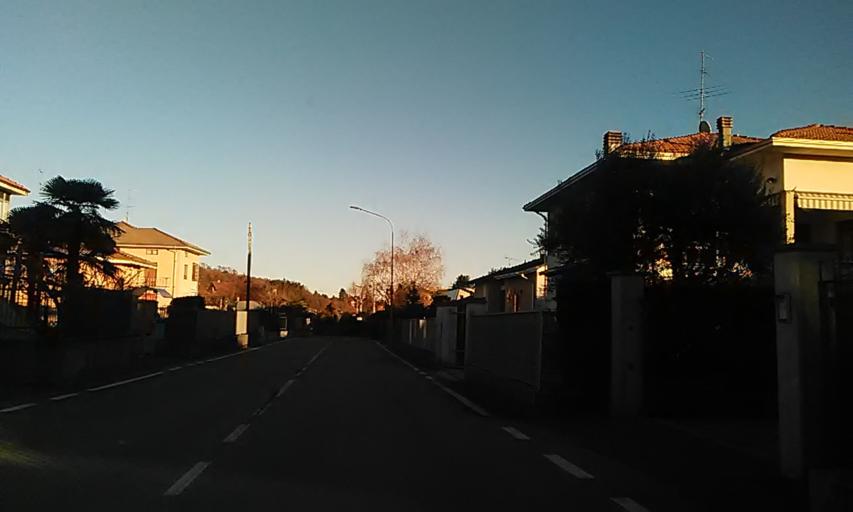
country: IT
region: Piedmont
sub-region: Provincia di Biella
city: Valdengo
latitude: 45.5677
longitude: 8.1388
